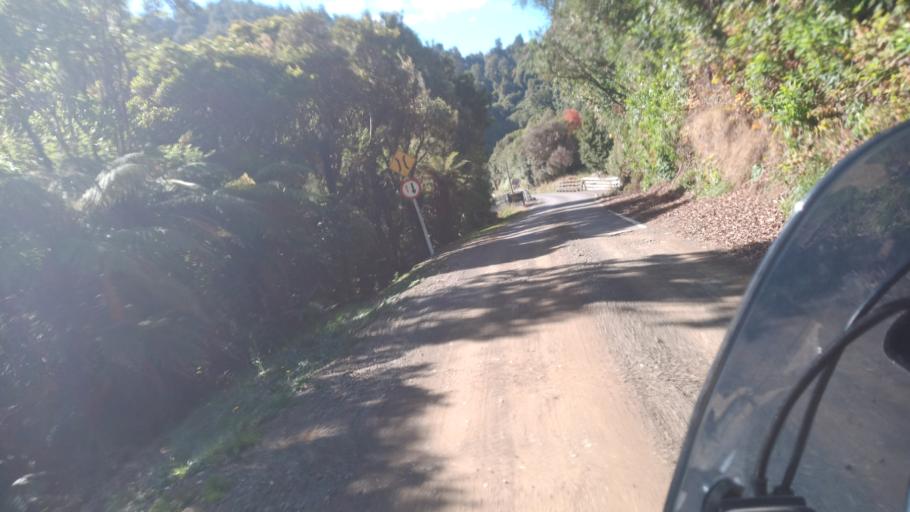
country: NZ
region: Bay of Plenty
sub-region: Opotiki District
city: Opotiki
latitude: -38.2496
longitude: 177.5901
